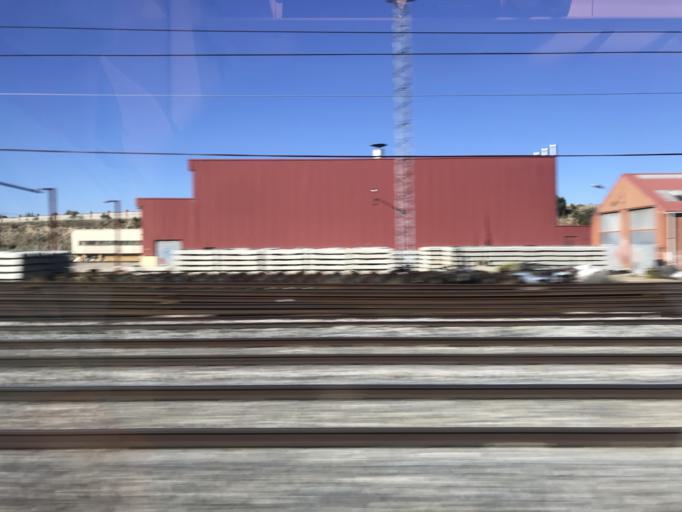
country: ES
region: Madrid
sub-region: Provincia de Madrid
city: Las Tablas
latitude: 40.5095
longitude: -3.6821
